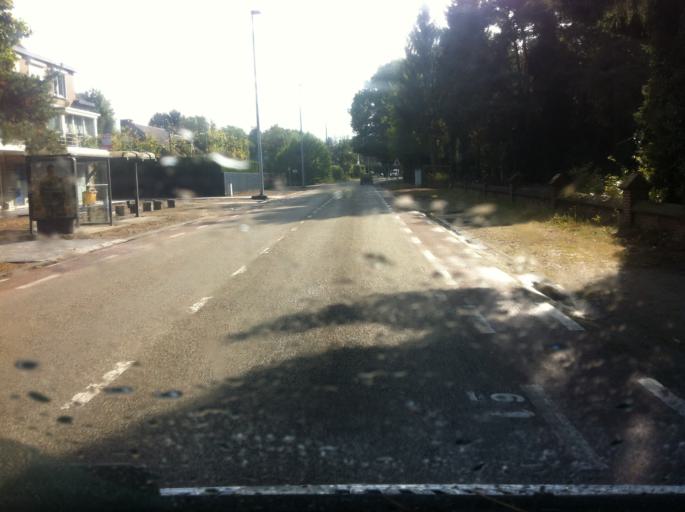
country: BE
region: Flanders
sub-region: Provincie Limburg
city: Maasmechelen
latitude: 50.9741
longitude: 5.6737
